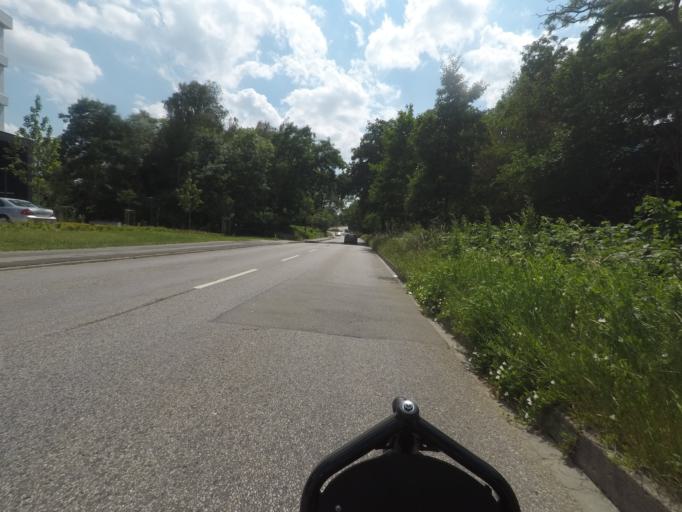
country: DE
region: Hamburg
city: Harburg
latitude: 53.4604
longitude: 9.9944
